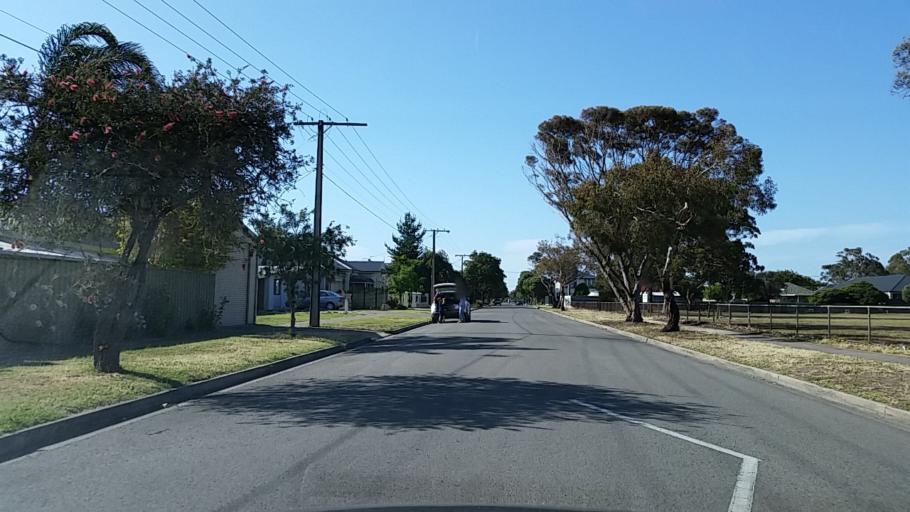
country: AU
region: South Australia
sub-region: Charles Sturt
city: Henley Beach
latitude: -34.9125
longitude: 138.5021
